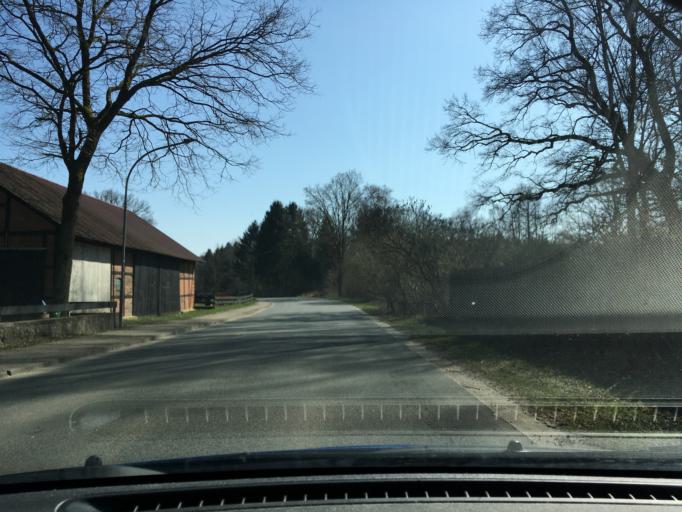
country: DE
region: Lower Saxony
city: Wriedel
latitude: 53.0749
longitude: 10.2826
